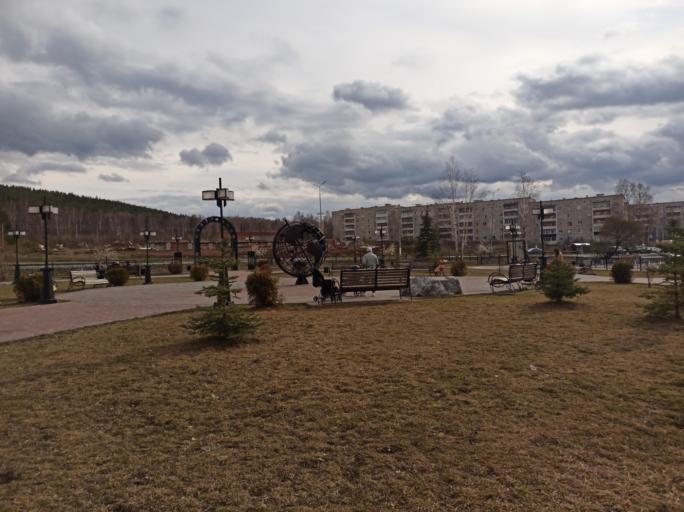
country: RU
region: Chelyabinsk
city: Satka
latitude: 55.0655
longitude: 58.9292
